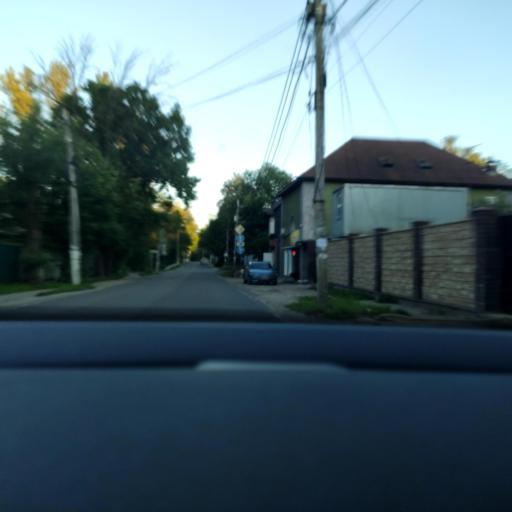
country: RU
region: Moskovskaya
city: Reutov
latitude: 55.7646
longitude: 37.8960
